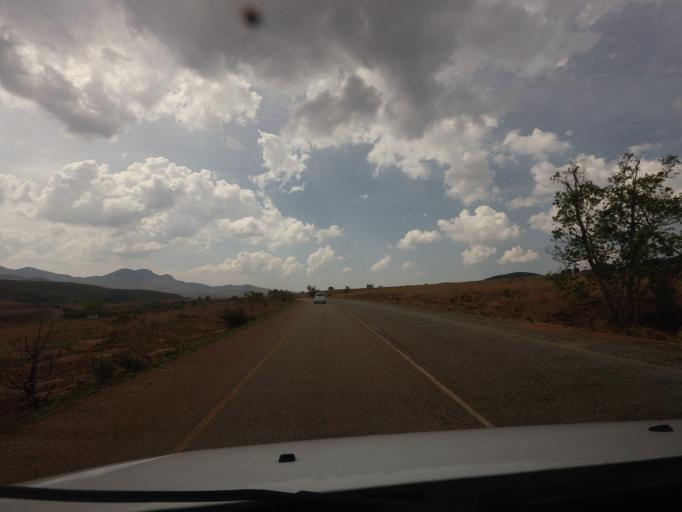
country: ZA
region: Mpumalanga
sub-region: Ehlanzeni District
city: Graksop
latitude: -24.7003
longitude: 30.8200
